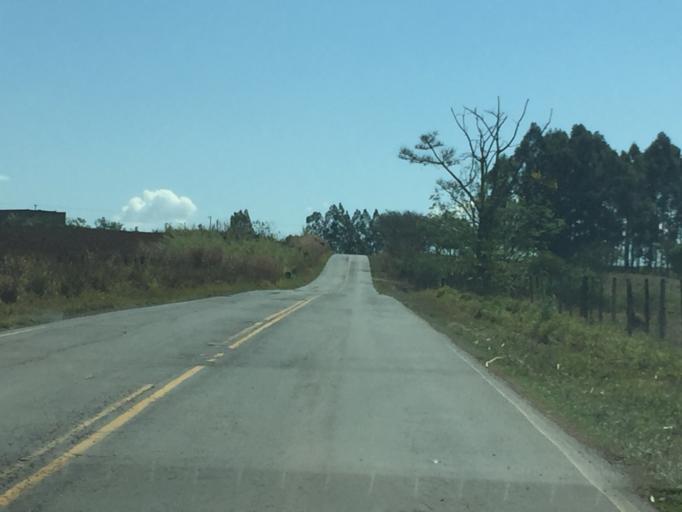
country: BR
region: Sao Paulo
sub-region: Moji-Guacu
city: Mogi-Gaucu
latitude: -22.3409
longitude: -46.8813
